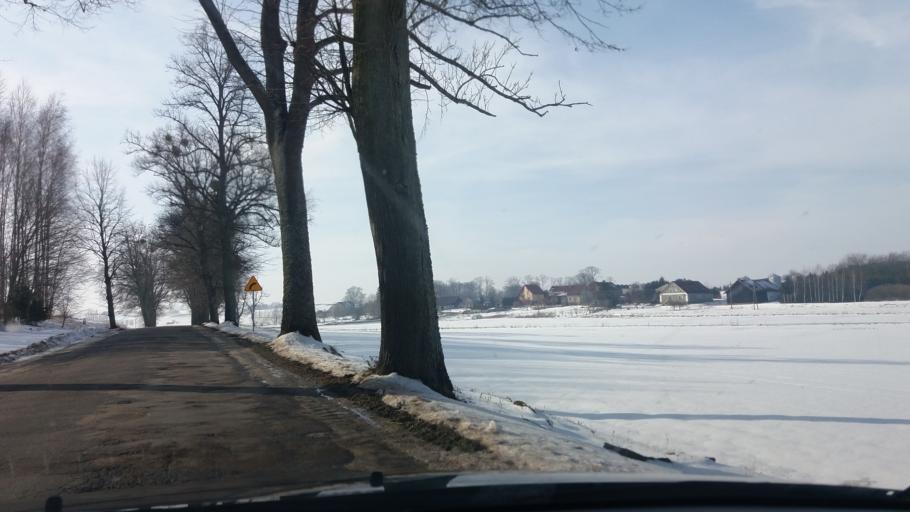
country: PL
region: Warmian-Masurian Voivodeship
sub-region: Powiat bartoszycki
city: Bisztynek
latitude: 54.1024
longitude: 20.8094
